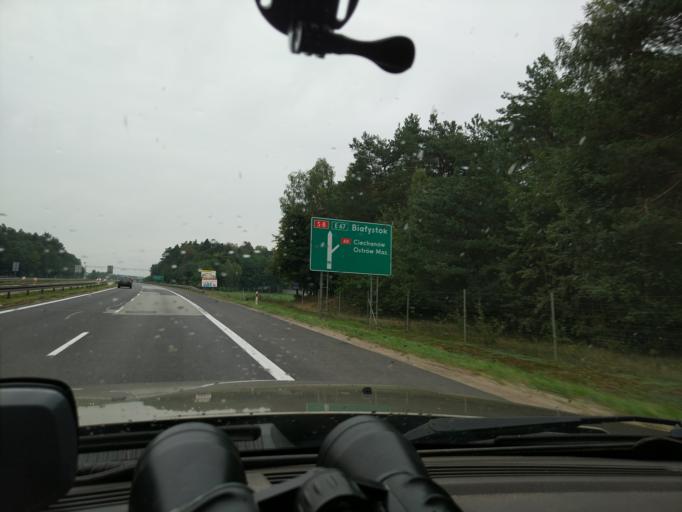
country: PL
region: Masovian Voivodeship
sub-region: Powiat ostrowski
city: Ostrow Mazowiecka
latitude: 52.7913
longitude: 21.8668
